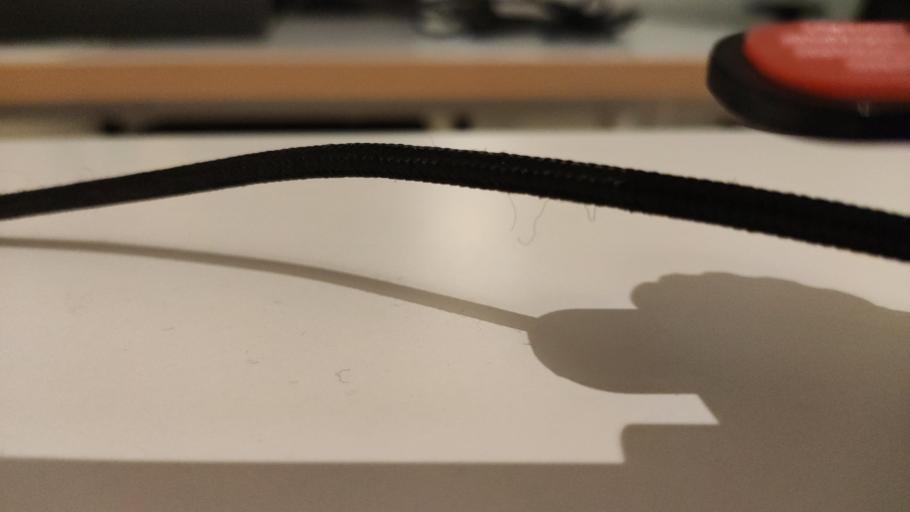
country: RU
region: Moskovskaya
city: Semkhoz
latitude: 56.4070
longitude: 38.0096
